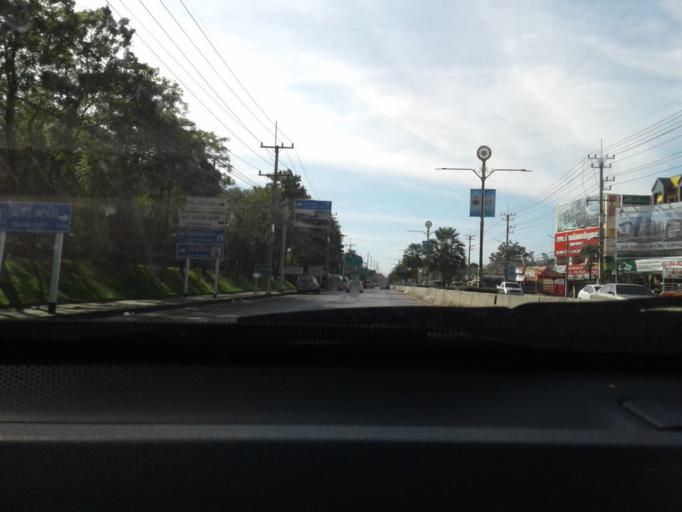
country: TH
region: Nakhon Pathom
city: Salaya
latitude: 13.8011
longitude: 100.3237
